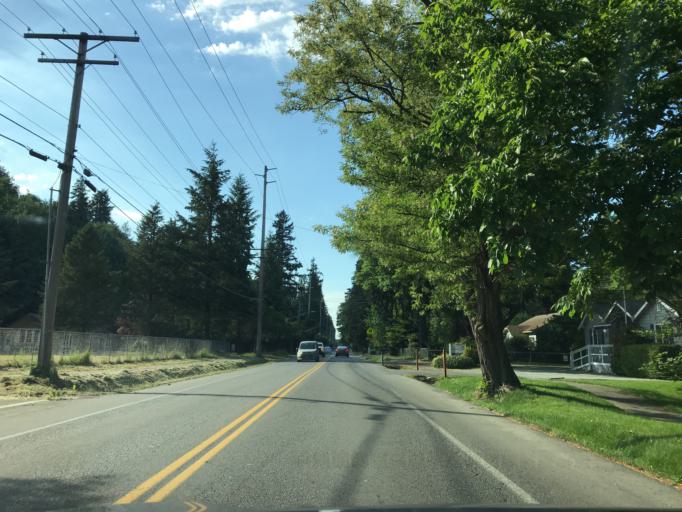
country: US
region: Washington
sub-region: King County
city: Issaquah
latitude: 47.5329
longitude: -122.0437
